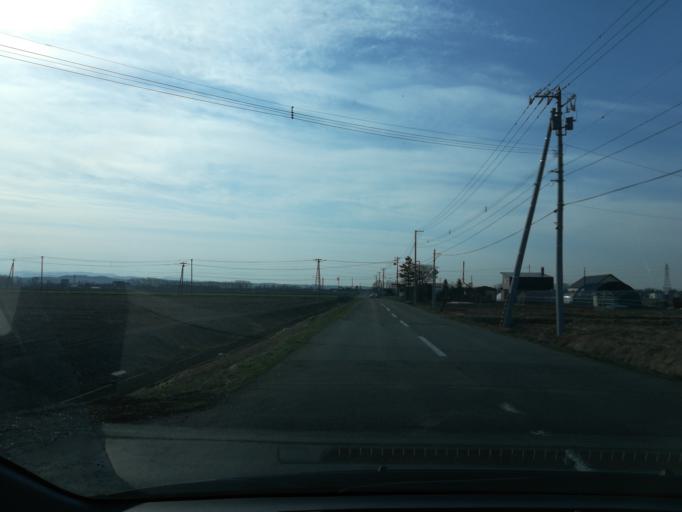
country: JP
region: Hokkaido
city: Iwamizawa
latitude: 43.1938
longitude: 141.7182
